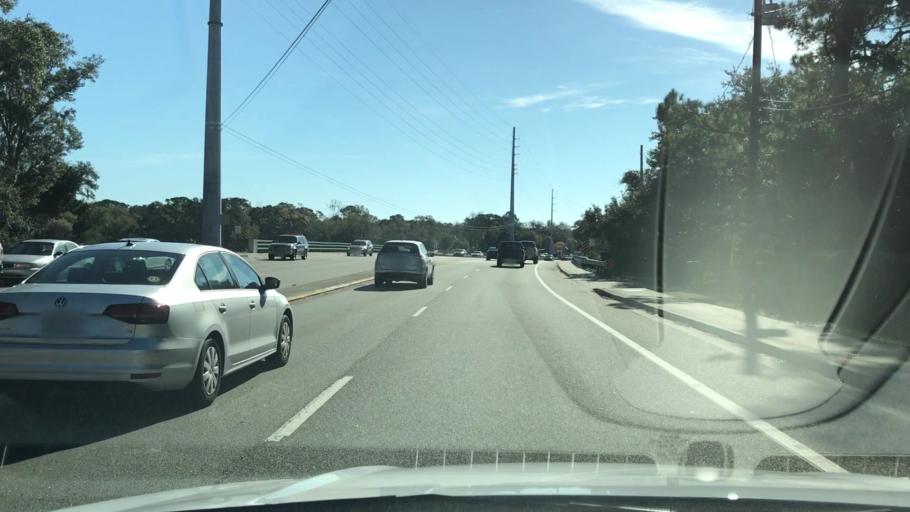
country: US
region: South Carolina
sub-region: Charleston County
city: Charleston
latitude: 32.7457
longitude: -79.9702
